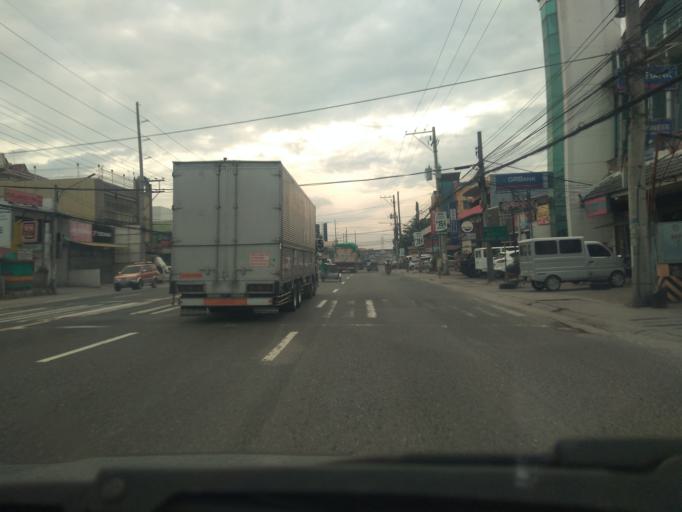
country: PH
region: Central Luzon
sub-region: Province of Pampanga
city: Magliman
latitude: 15.0408
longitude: 120.6783
